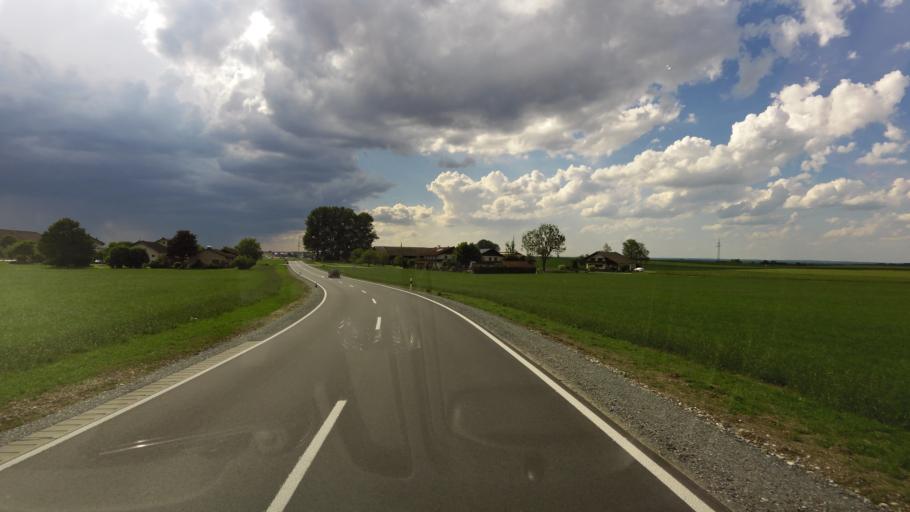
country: DE
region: Bavaria
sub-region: Upper Bavaria
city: Griesstatt
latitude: 47.9876
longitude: 12.1986
